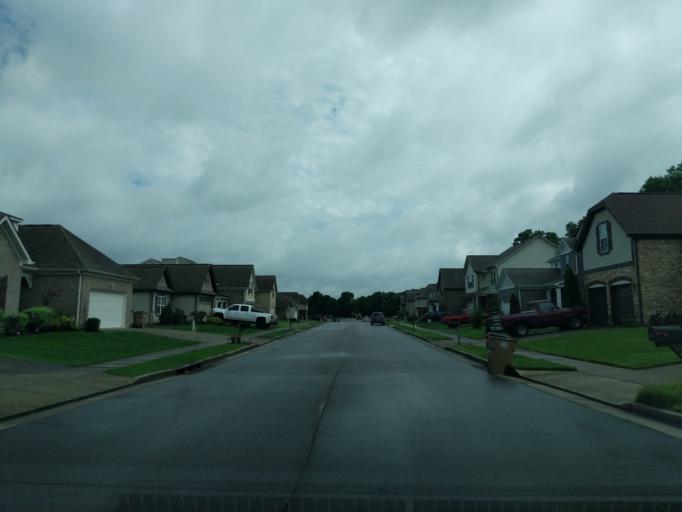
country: US
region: Tennessee
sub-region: Davidson County
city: Lakewood
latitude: 36.2389
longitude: -86.6907
